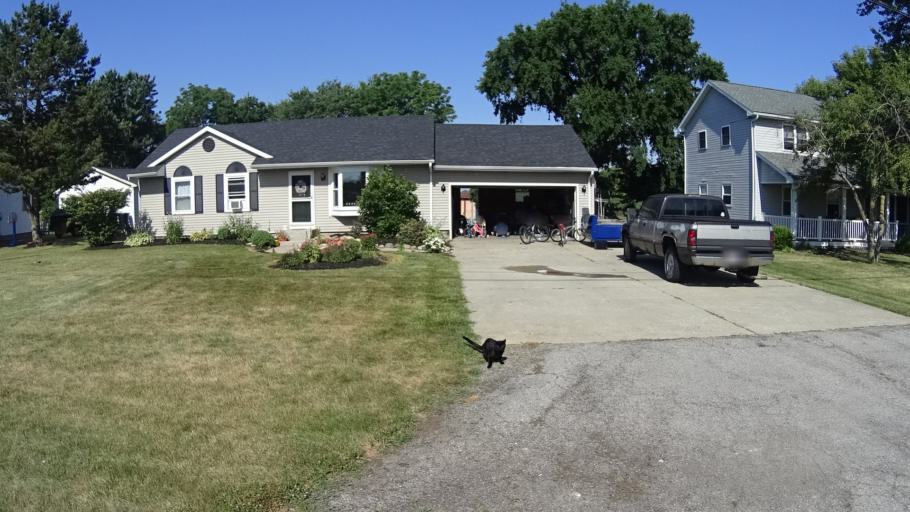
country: US
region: Ohio
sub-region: Huron County
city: Bellevue
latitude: 41.3711
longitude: -82.8021
